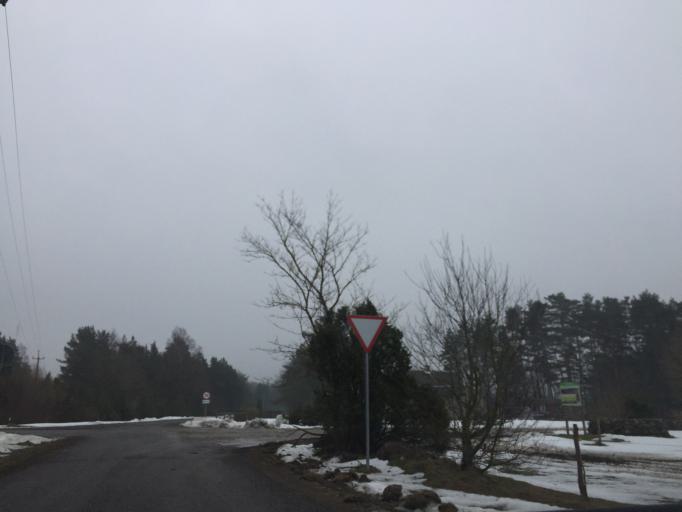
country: EE
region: Saare
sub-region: Kuressaare linn
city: Kuressaare
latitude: 58.2700
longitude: 22.5853
